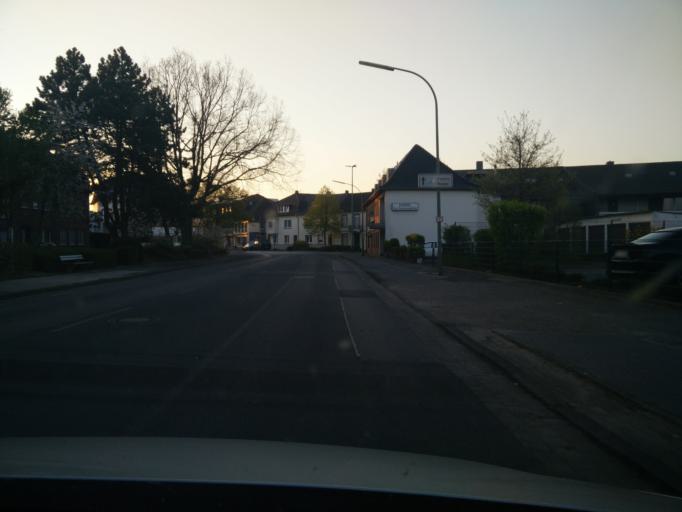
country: DE
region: North Rhine-Westphalia
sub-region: Regierungsbezirk Dusseldorf
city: Goch
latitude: 51.6734
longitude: 6.1633
